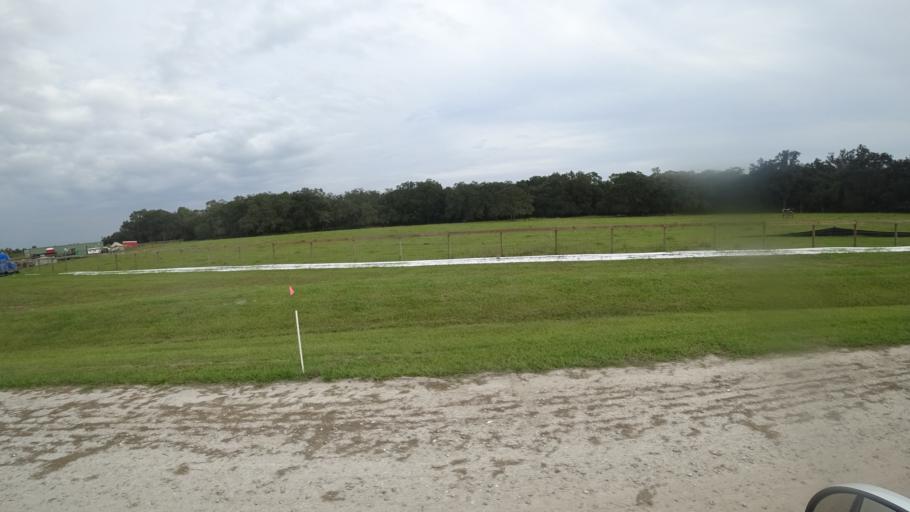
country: US
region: Florida
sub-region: Sarasota County
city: Lake Sarasota
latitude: 27.2899
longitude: -82.2165
